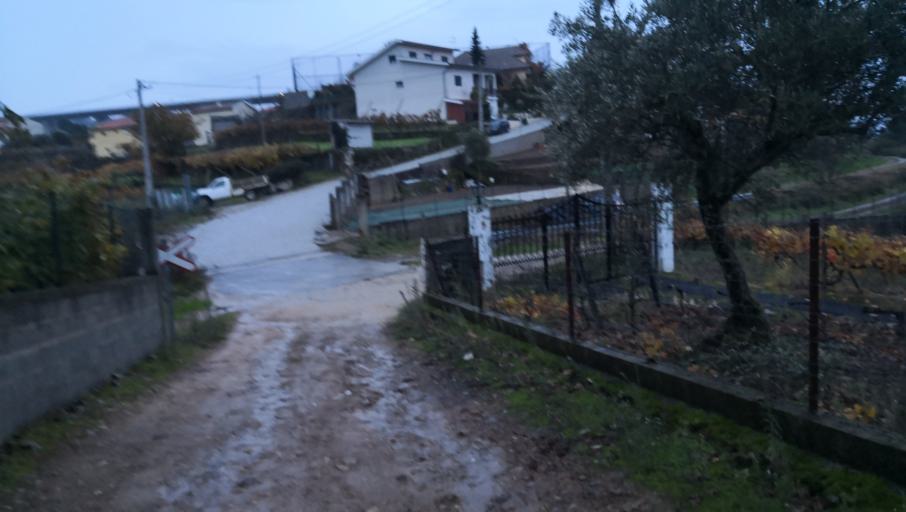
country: PT
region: Vila Real
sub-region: Vila Real
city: Vila Real
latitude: 41.2811
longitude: -7.7468
